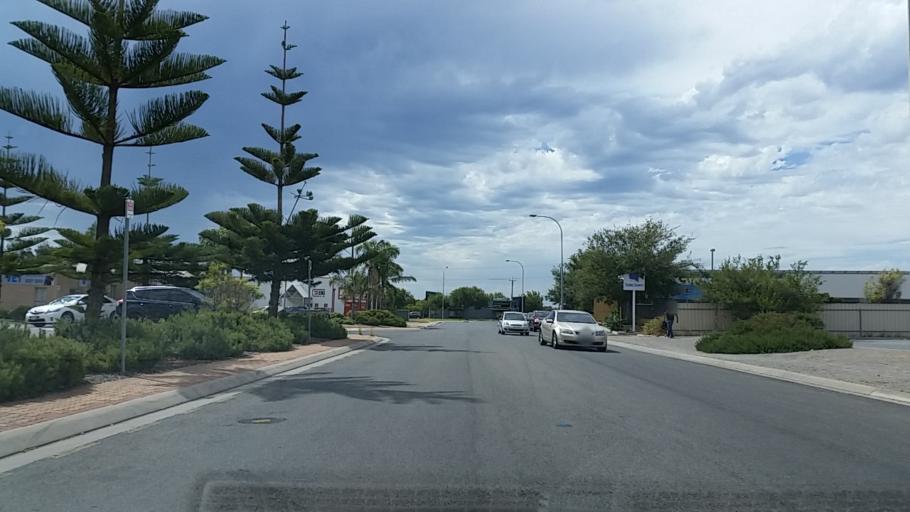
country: AU
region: South Australia
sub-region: Onkaparinga
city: Moana
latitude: -35.1926
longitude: 138.4791
